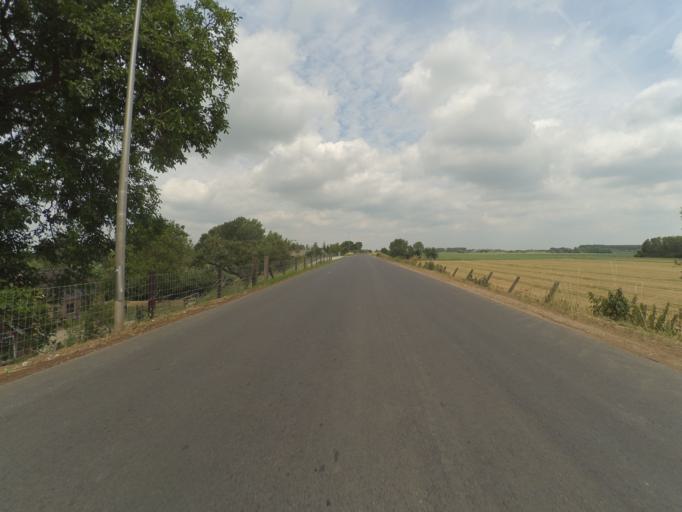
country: NL
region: Gelderland
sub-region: Gemeente Culemborg
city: Culemborg
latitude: 51.9451
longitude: 5.1613
